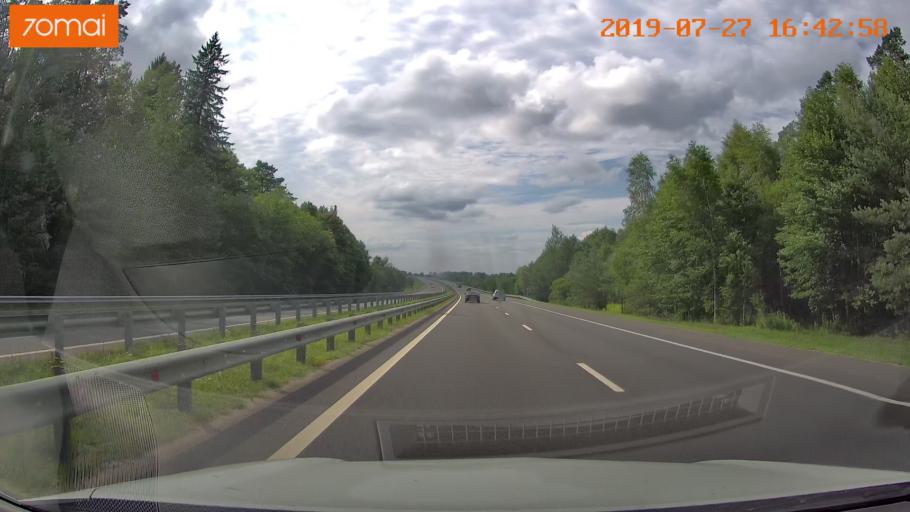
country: RU
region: Kaliningrad
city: Gvardeysk
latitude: 54.6684
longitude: 21.1141
